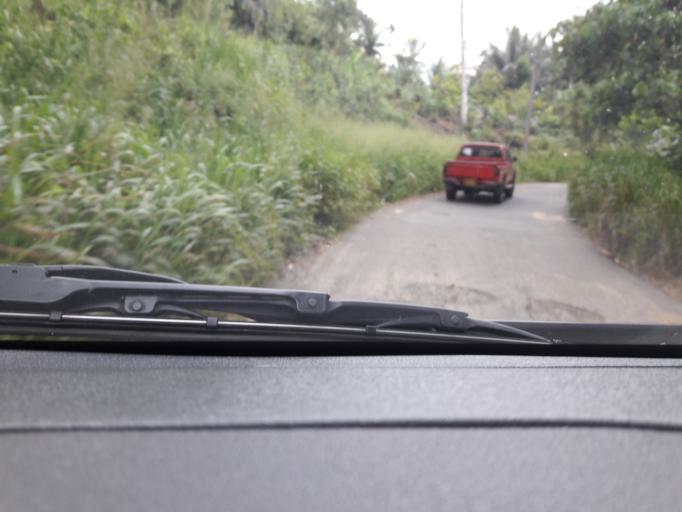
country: LK
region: Southern
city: Galle
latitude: 6.1924
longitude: 80.3037
